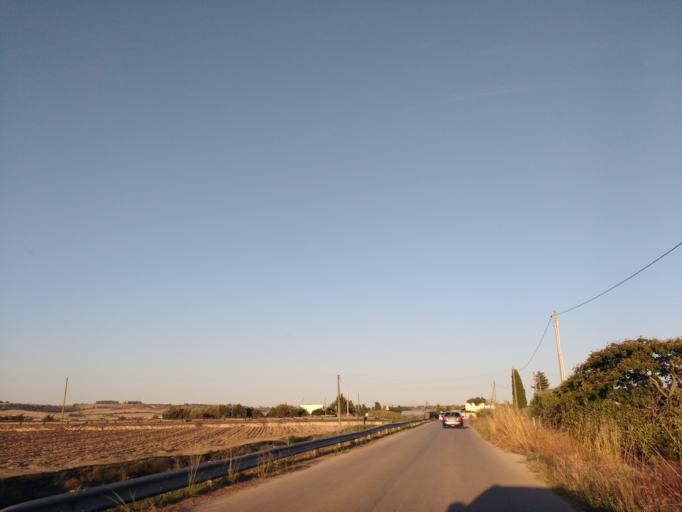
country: IT
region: Sicily
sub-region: Ragusa
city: Ispica
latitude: 36.7338
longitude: 14.9262
